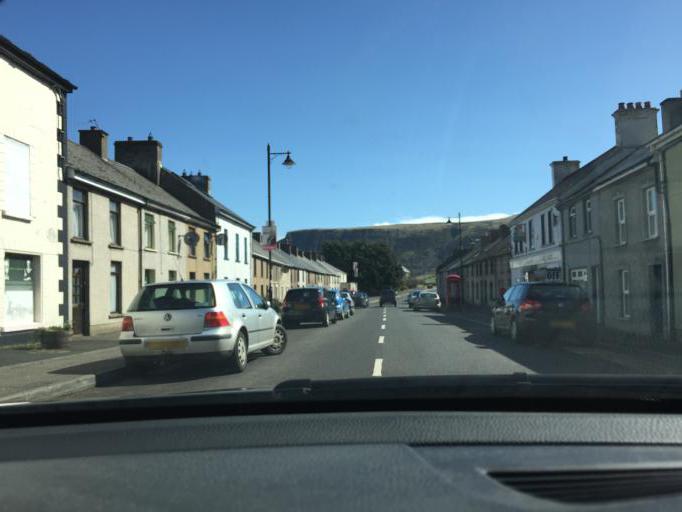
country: GB
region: Northern Ireland
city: Glenariff
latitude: 55.0611
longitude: -6.0601
